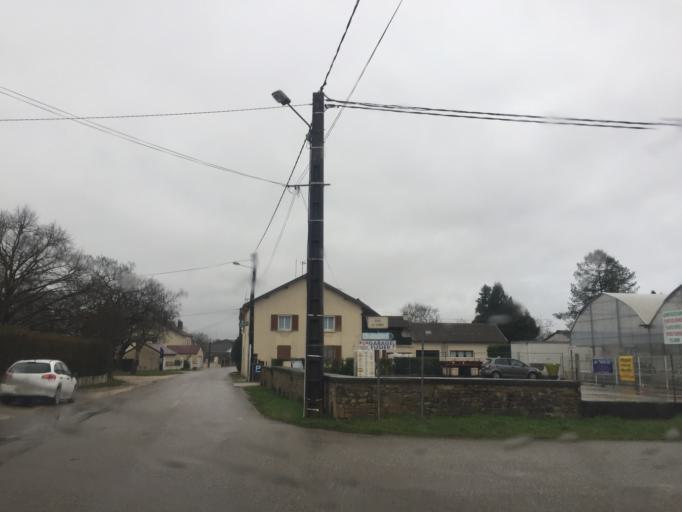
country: FR
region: Franche-Comte
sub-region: Departement du Jura
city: Dole
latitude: 47.1005
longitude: 5.5369
